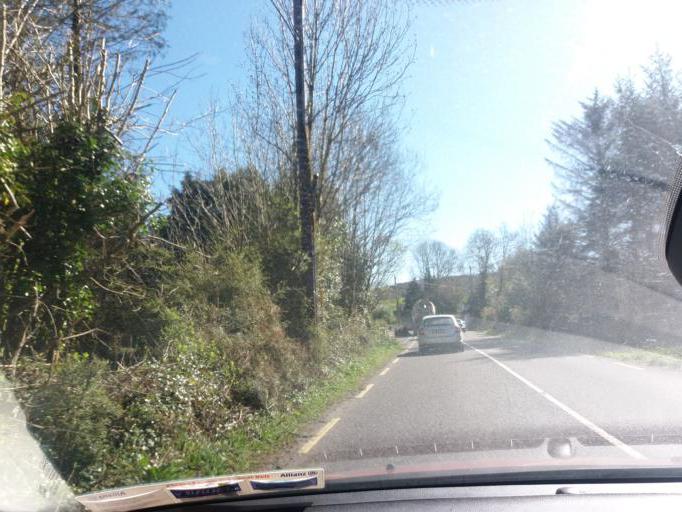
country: IE
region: Munster
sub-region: Ciarrai
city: Cill Airne
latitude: 51.9802
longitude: -9.3195
